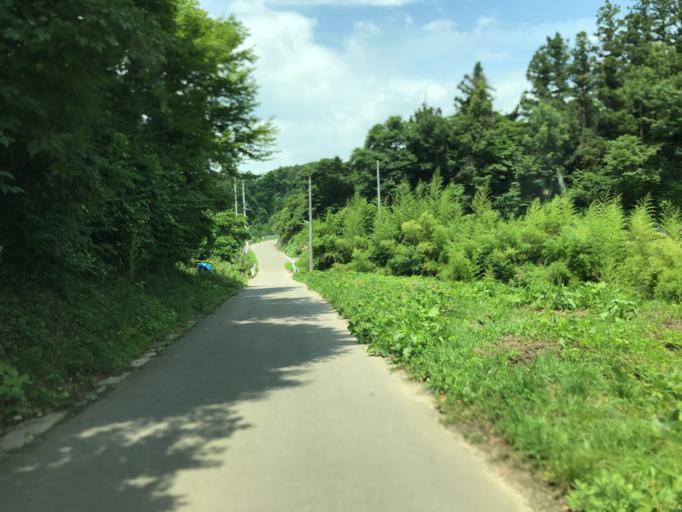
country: JP
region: Fukushima
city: Fukushima-shi
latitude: 37.6711
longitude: 140.5068
